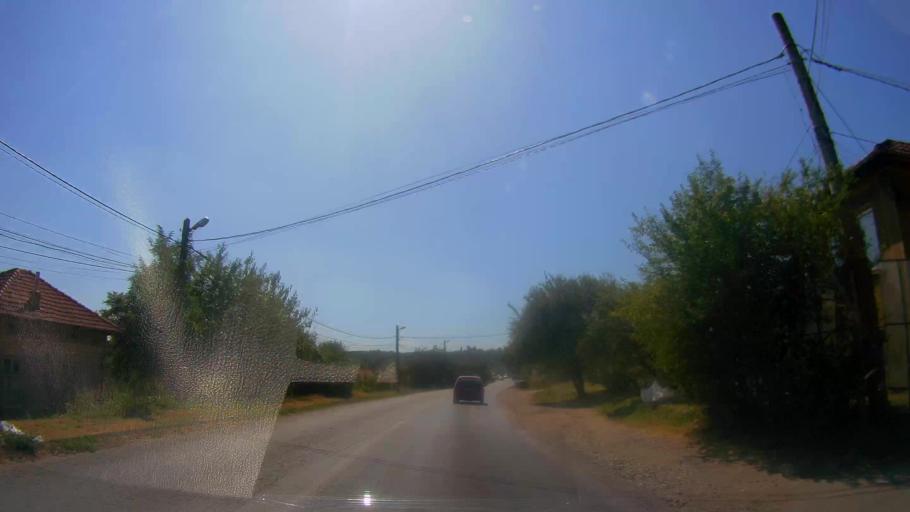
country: BG
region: Veliko Turnovo
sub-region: Obshtina Gorna Oryakhovitsa
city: Purvomaytsi
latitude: 43.1733
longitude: 25.6206
